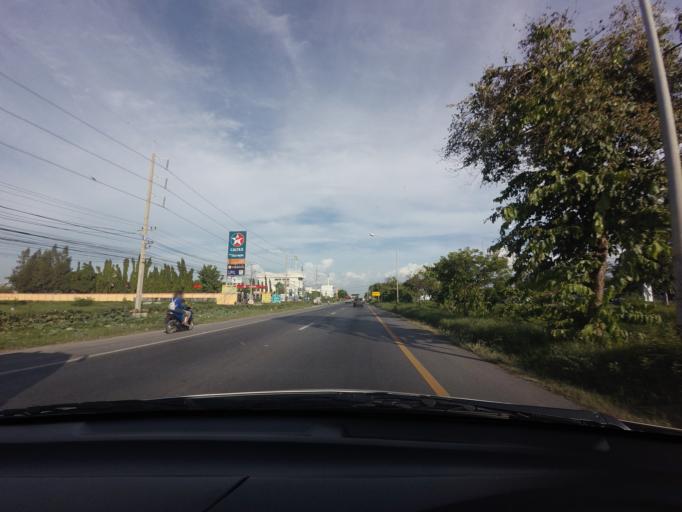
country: TH
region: Pathum Thani
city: Lat Lum Kaeo
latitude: 14.0261
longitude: 100.3549
